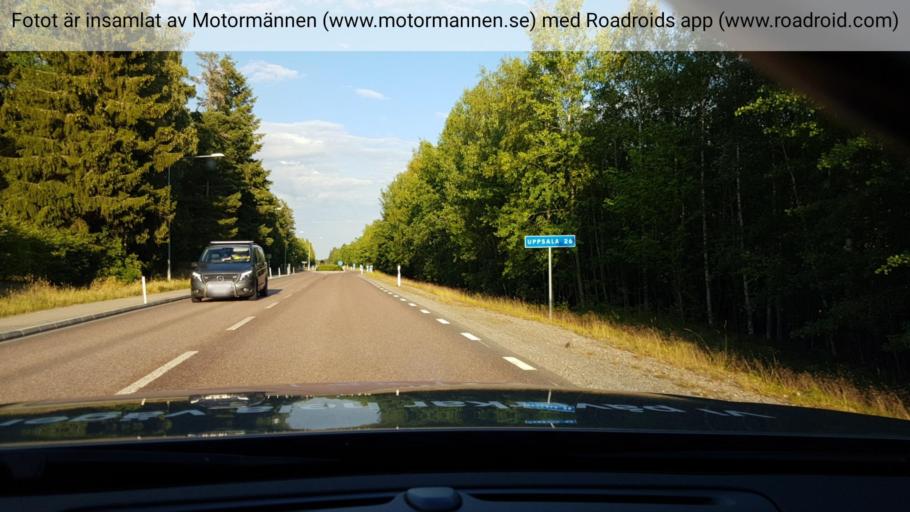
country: SE
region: Uppsala
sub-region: Enkopings Kommun
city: Orsundsbro
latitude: 59.8848
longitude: 17.2080
